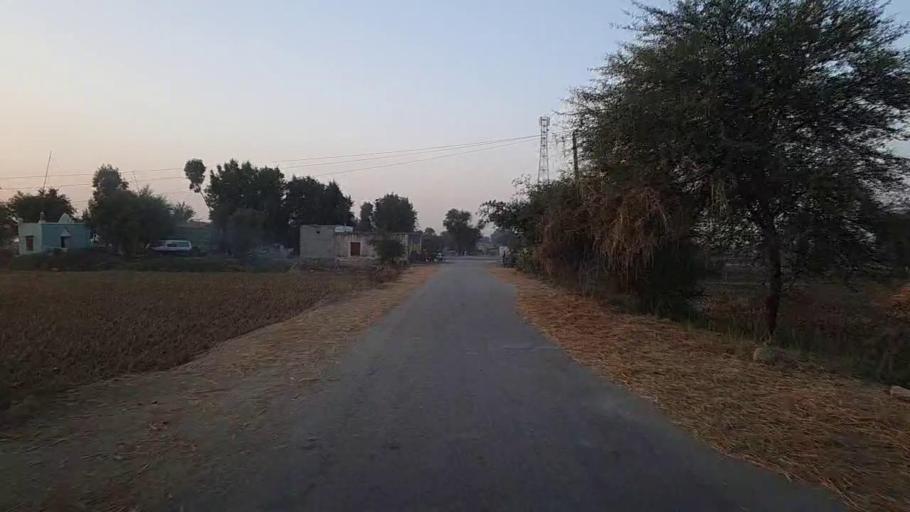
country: PK
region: Sindh
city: Kashmor
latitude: 28.4171
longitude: 69.4506
